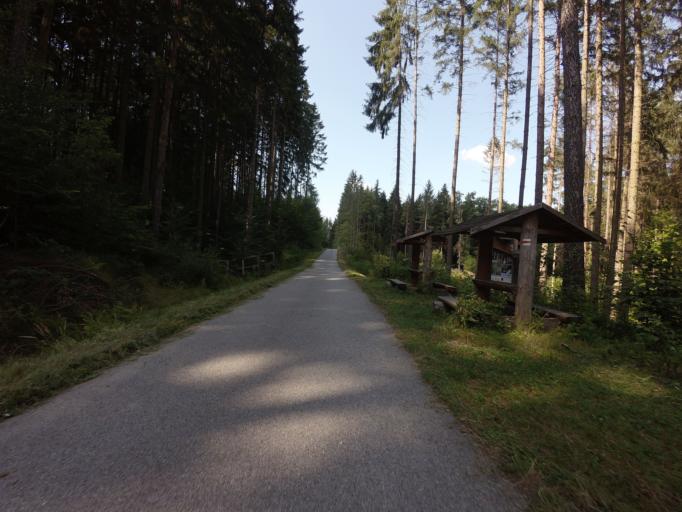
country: CZ
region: Jihocesky
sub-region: Okres Ceske Budejovice
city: Hluboka nad Vltavou
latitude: 49.1014
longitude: 14.4629
